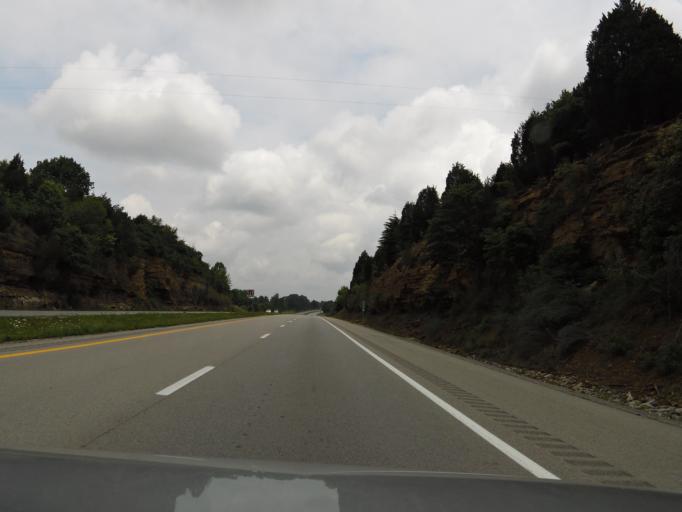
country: US
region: Kentucky
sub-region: Grayson County
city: Leitchfield
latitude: 37.5183
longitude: -86.1486
